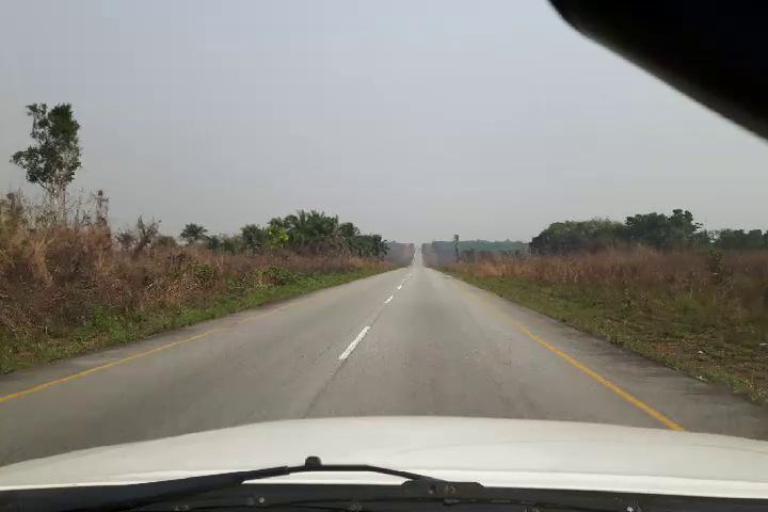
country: SL
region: Southern Province
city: Largo
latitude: 8.2367
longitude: -12.0829
